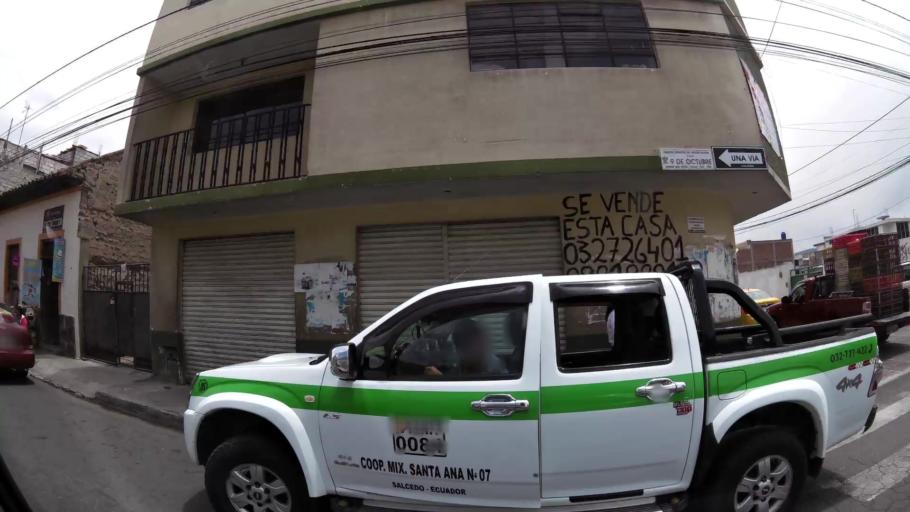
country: EC
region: Cotopaxi
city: San Miguel de Salcedo
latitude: -1.0440
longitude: -78.5919
